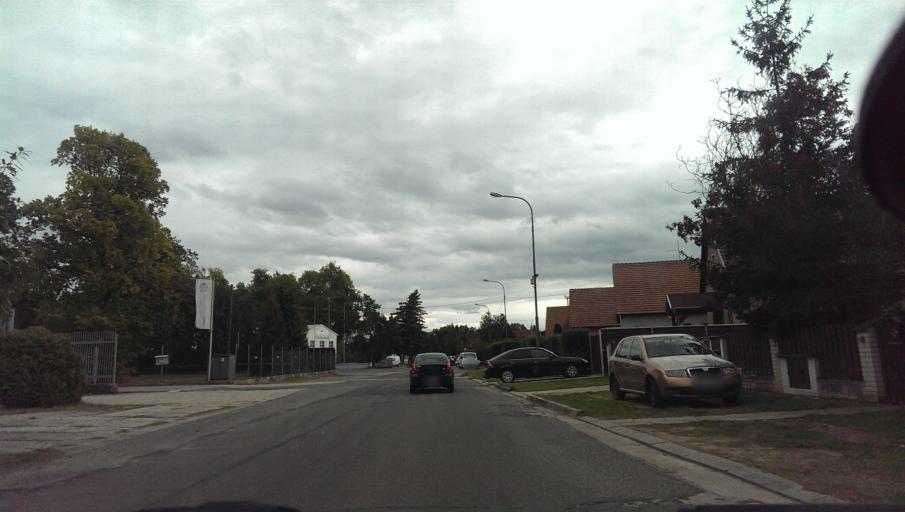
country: CZ
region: South Moravian
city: Moravsky Pisek
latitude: 48.9812
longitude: 17.3134
